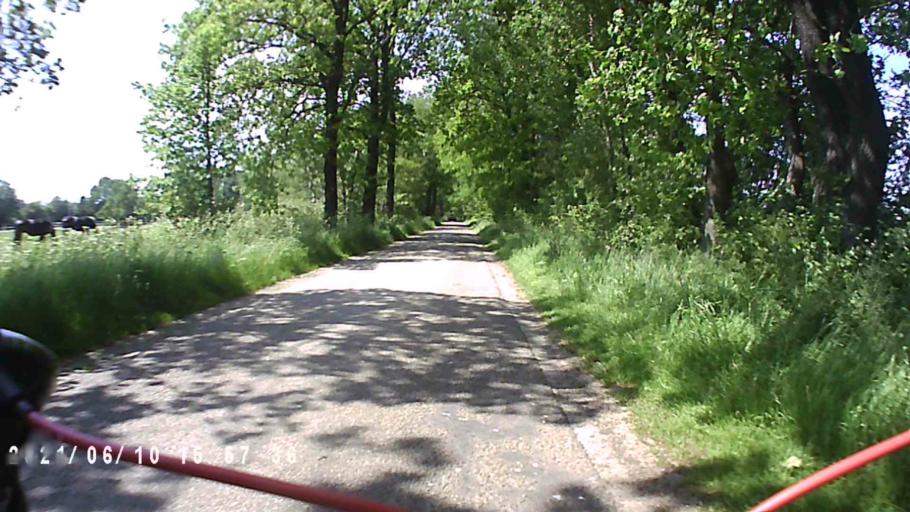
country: NL
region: Friesland
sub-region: Gemeente Achtkarspelen
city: Drogeham
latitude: 53.1895
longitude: 6.0943
